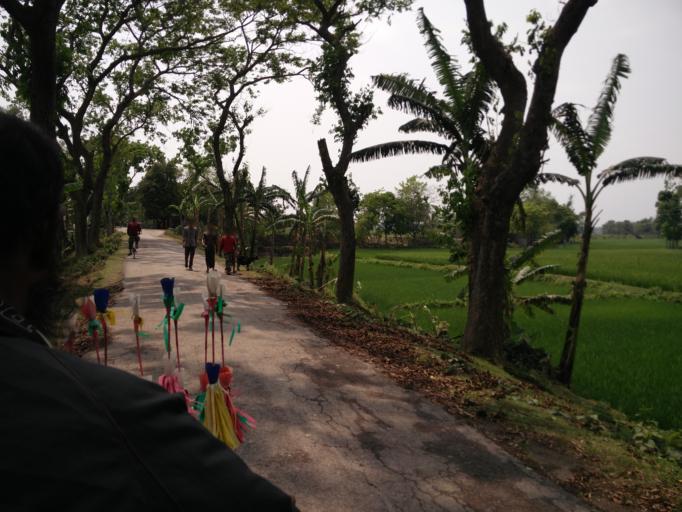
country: BD
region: Dhaka
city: Sherpur
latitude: 24.9382
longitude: 90.1596
